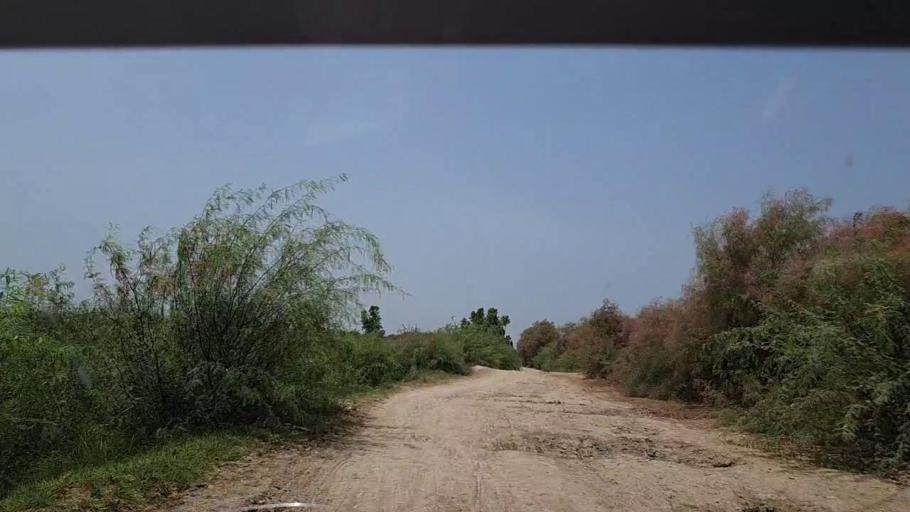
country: PK
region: Sindh
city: Adilpur
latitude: 27.9018
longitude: 69.2300
